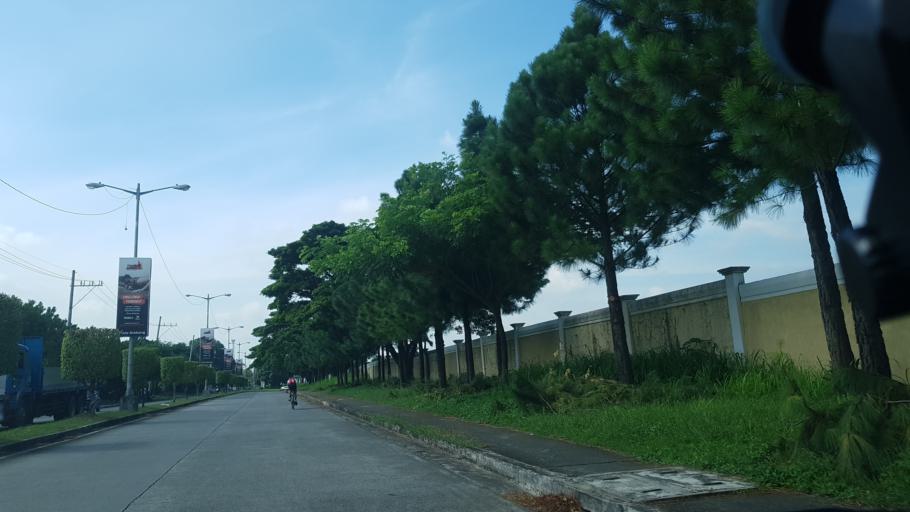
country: PH
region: Calabarzon
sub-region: Province of Laguna
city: Magsaysay
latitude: 14.3563
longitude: 121.0092
